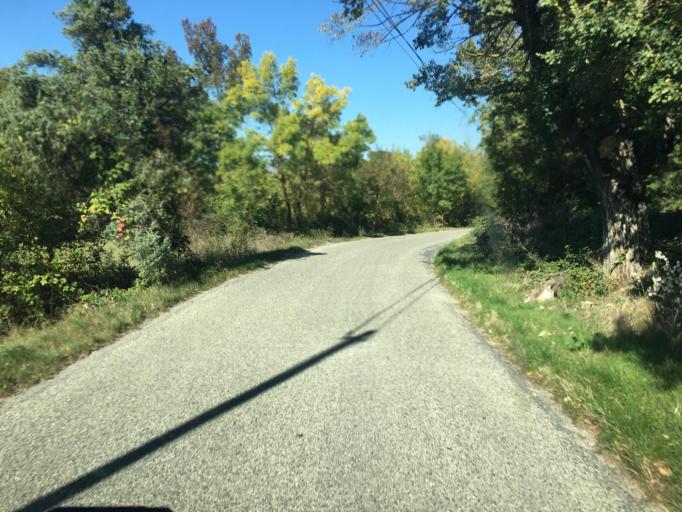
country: FR
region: Languedoc-Roussillon
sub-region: Departement du Gard
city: Mons
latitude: 44.1618
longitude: 4.3136
